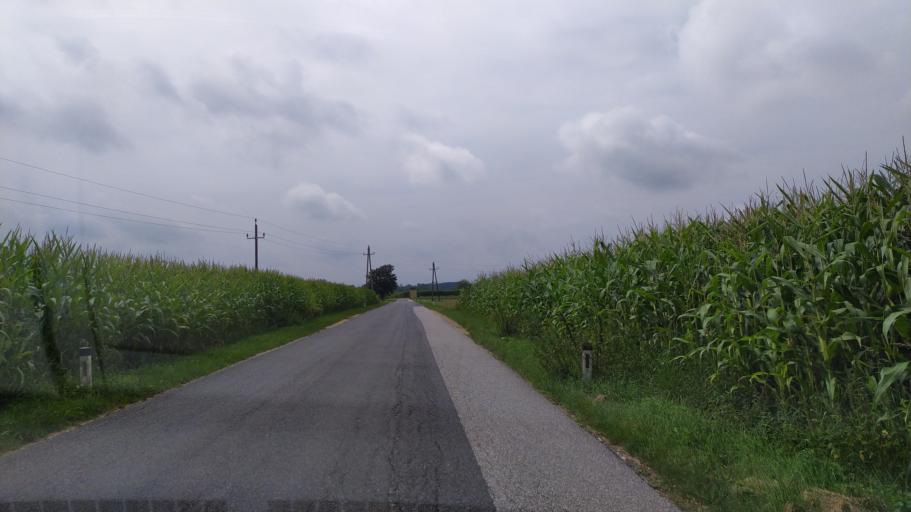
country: AT
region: Upper Austria
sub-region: Politischer Bezirk Perg
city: Bad Kreuzen
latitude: 48.1973
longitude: 14.7777
